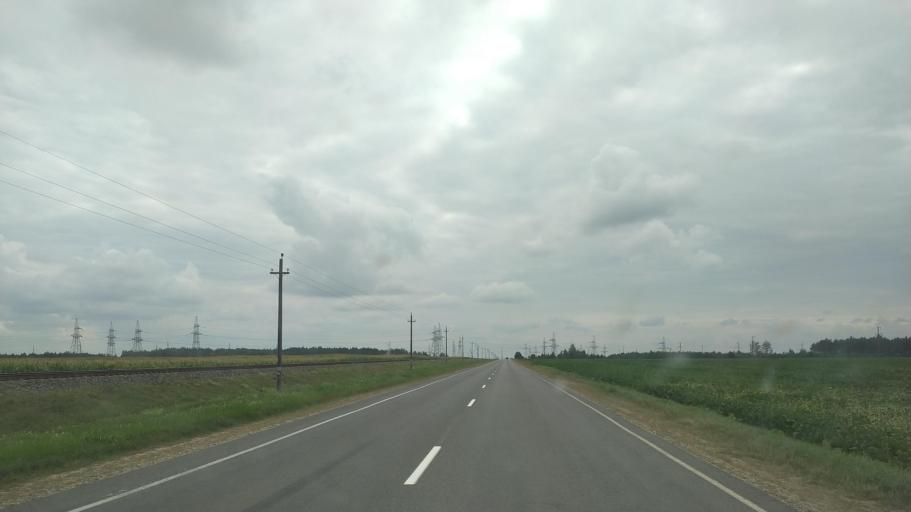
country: BY
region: Brest
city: Byelaazyorsk
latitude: 52.5217
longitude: 25.1499
